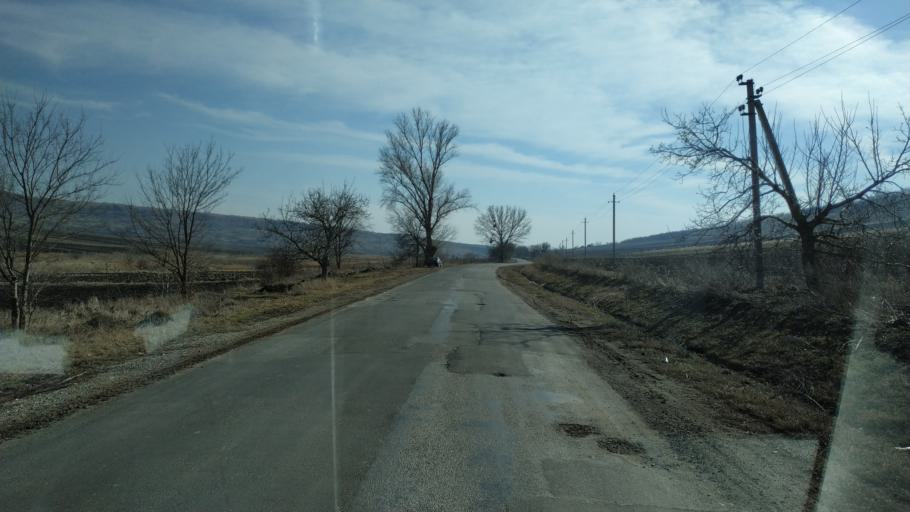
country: MD
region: Nisporeni
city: Nisporeni
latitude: 47.1408
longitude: 28.1144
